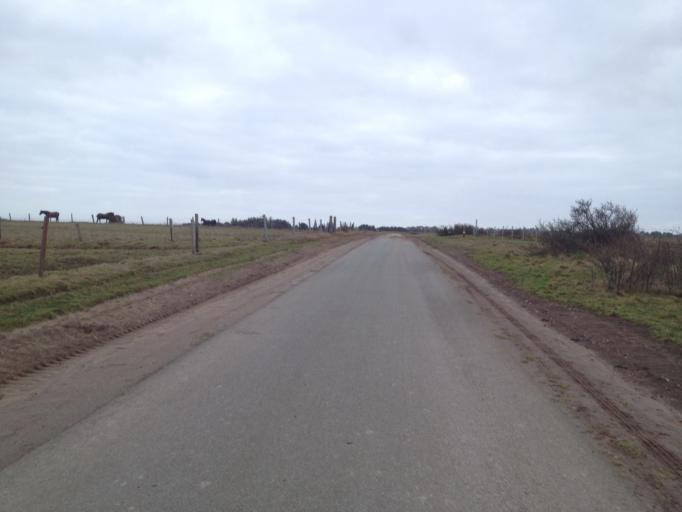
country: DE
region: Schleswig-Holstein
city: Nebel
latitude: 54.6616
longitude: 8.3477
